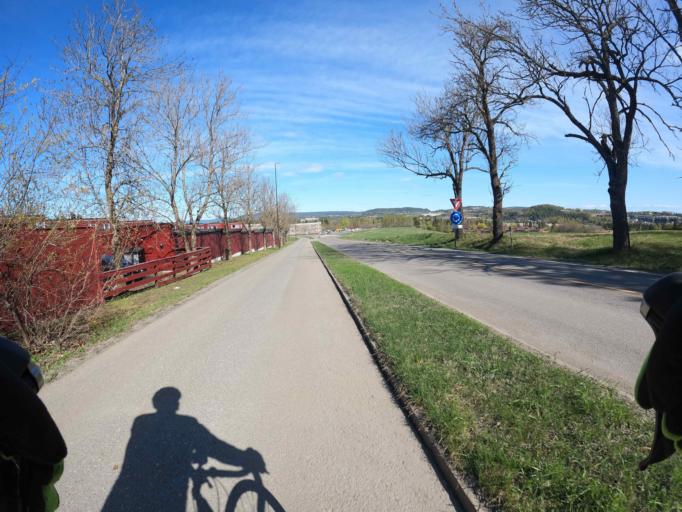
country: NO
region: Akershus
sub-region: Skedsmo
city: Lillestrom
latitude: 59.9667
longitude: 11.0080
